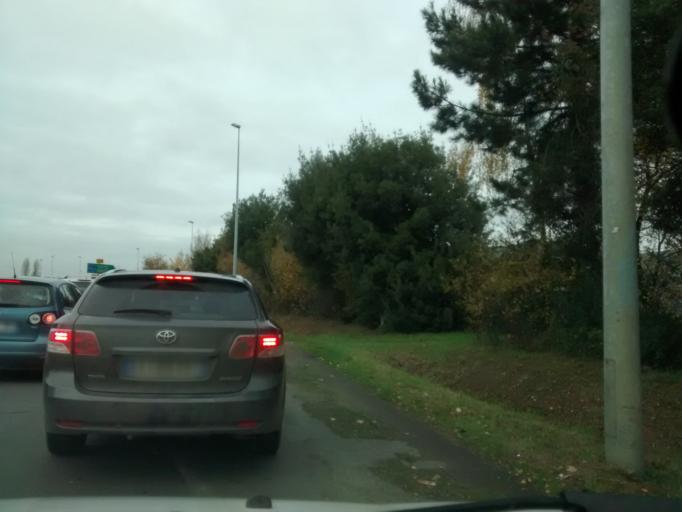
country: FR
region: Brittany
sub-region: Departement d'Ille-et-Vilaine
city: Saint-Gregoire
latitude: 48.1345
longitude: -1.6912
